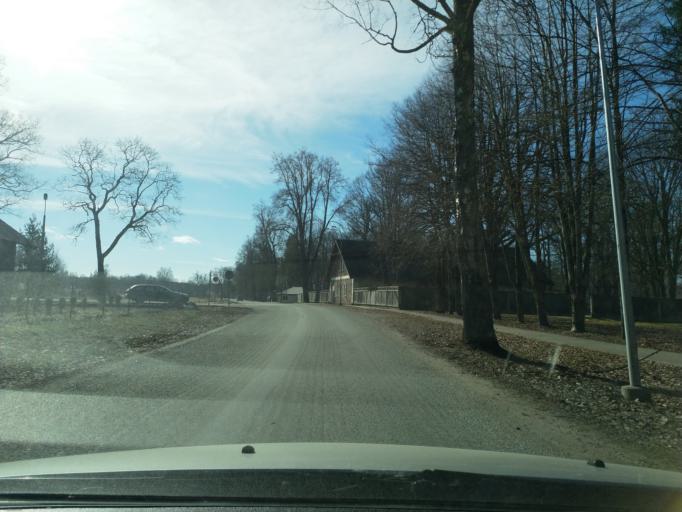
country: LV
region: Valmieras Rajons
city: Valmiera
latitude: 57.5229
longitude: 25.4204
